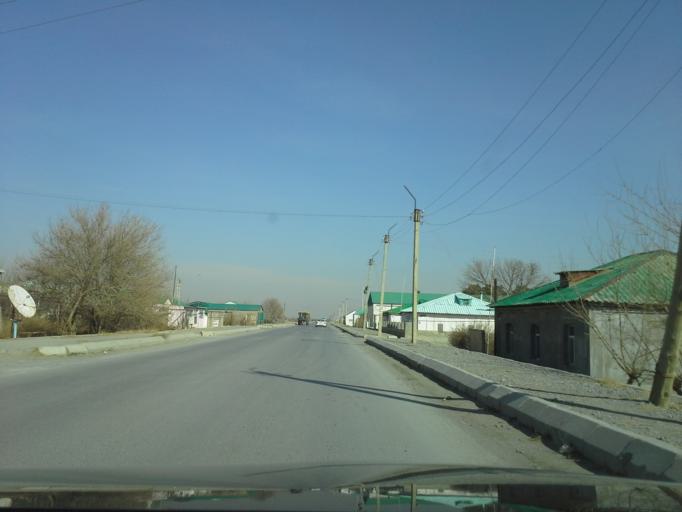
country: TM
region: Ahal
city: Abadan
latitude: 38.1111
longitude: 58.0336
